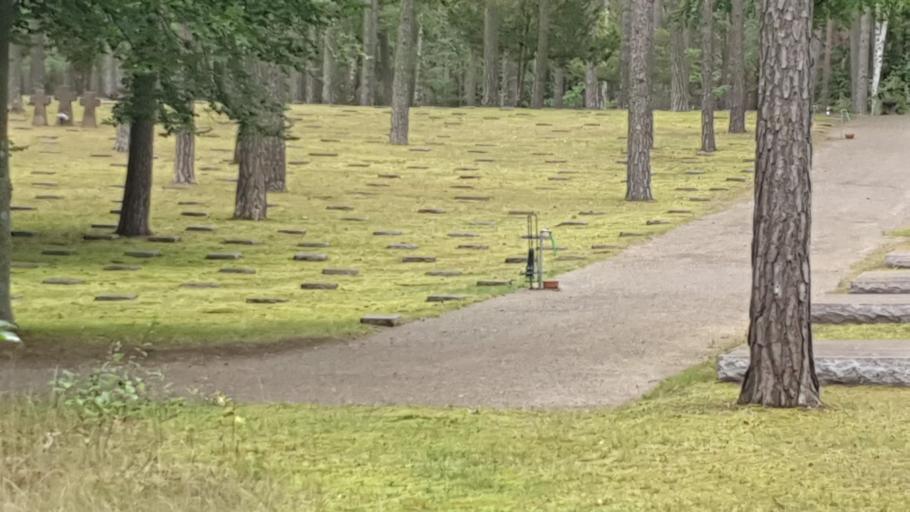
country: DE
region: Brandenburg
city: Halbe
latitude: 52.1022
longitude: 13.6907
